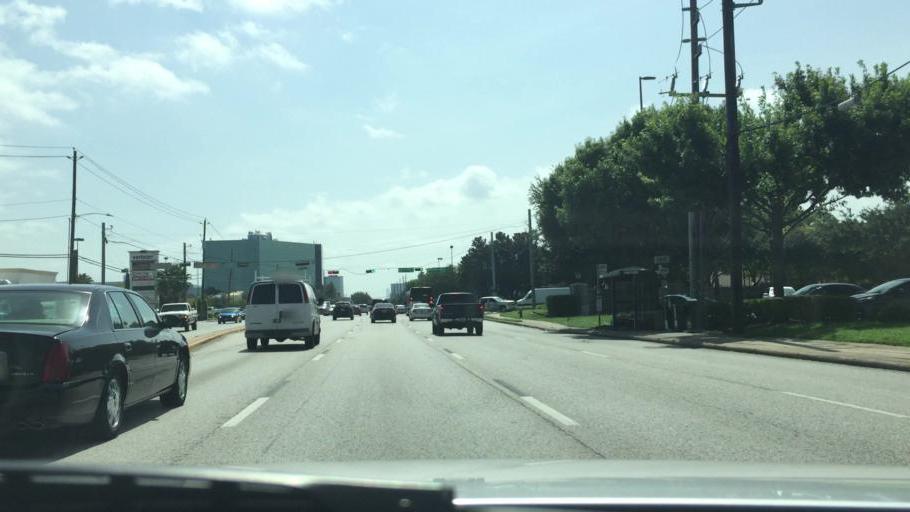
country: US
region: Texas
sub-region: Harris County
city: Bunker Hill Village
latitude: 29.7365
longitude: -95.5861
